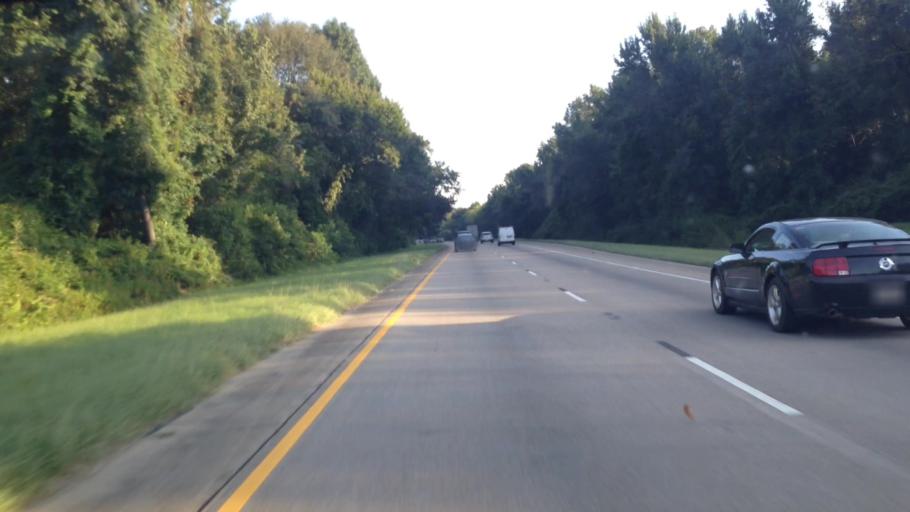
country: US
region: Louisiana
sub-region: Ascension Parish
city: Prairieville
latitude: 30.3006
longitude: -90.9922
